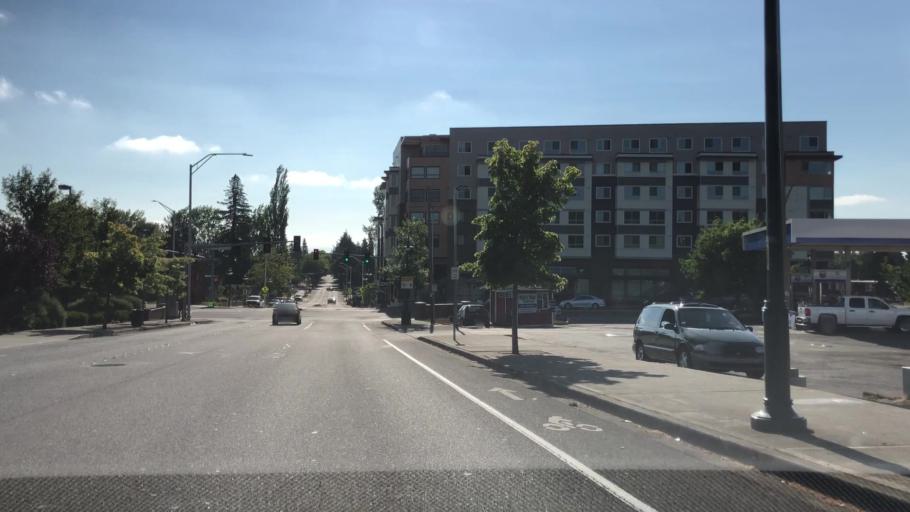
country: US
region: Washington
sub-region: King County
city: Riverton
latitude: 47.4742
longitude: -122.2855
